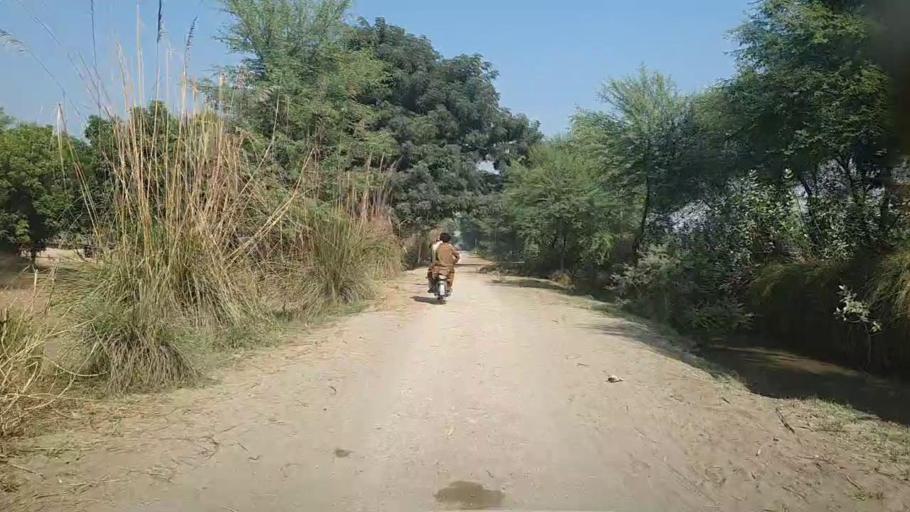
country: PK
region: Sindh
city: Karaundi
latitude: 26.9623
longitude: 68.4211
